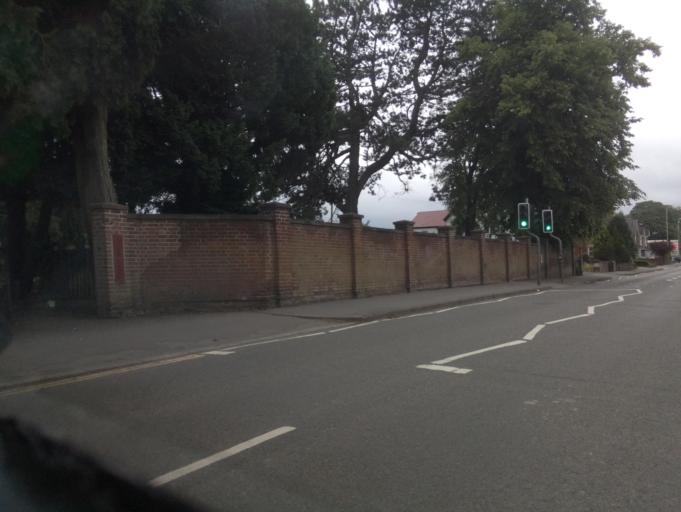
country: GB
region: England
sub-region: Leicestershire
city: Coalville
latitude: 52.7224
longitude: -1.3647
